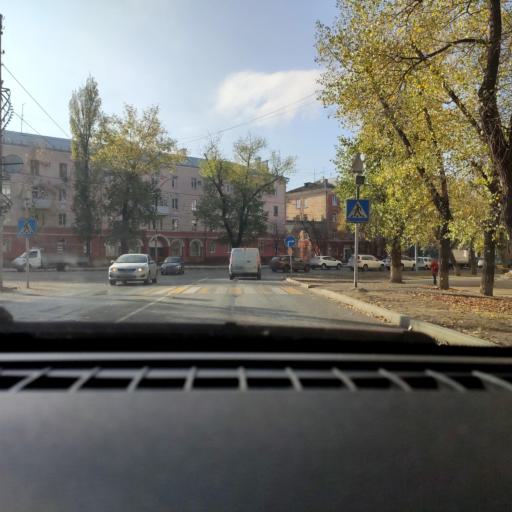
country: RU
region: Voronezj
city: Voronezh
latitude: 51.6347
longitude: 39.2370
